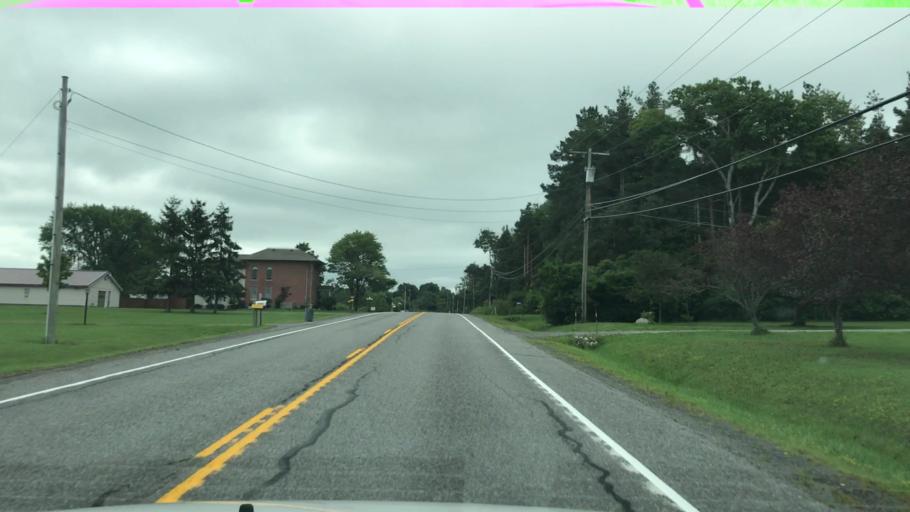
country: US
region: New York
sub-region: Wyoming County
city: Attica
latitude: 42.8362
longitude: -78.3438
